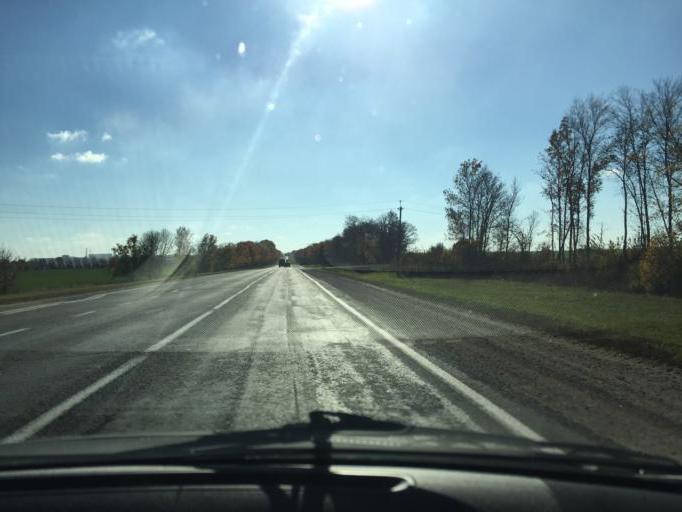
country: BY
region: Minsk
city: Salihorsk
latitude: 52.8931
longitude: 27.4730
